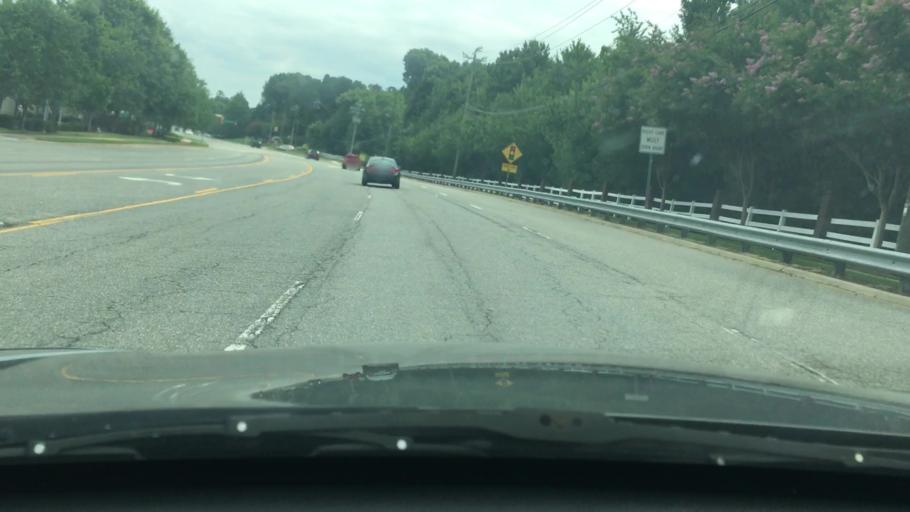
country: US
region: North Carolina
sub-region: Wake County
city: West Raleigh
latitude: 35.8588
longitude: -78.7130
